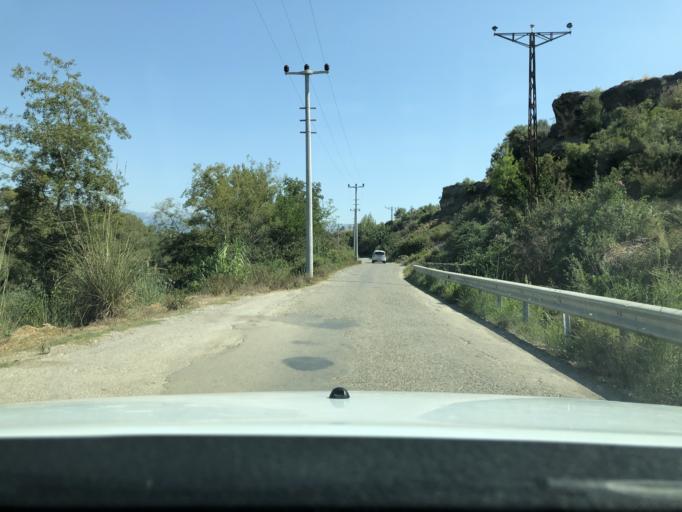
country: TR
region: Antalya
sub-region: Manavgat
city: Manavgat
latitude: 36.7999
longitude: 31.4680
